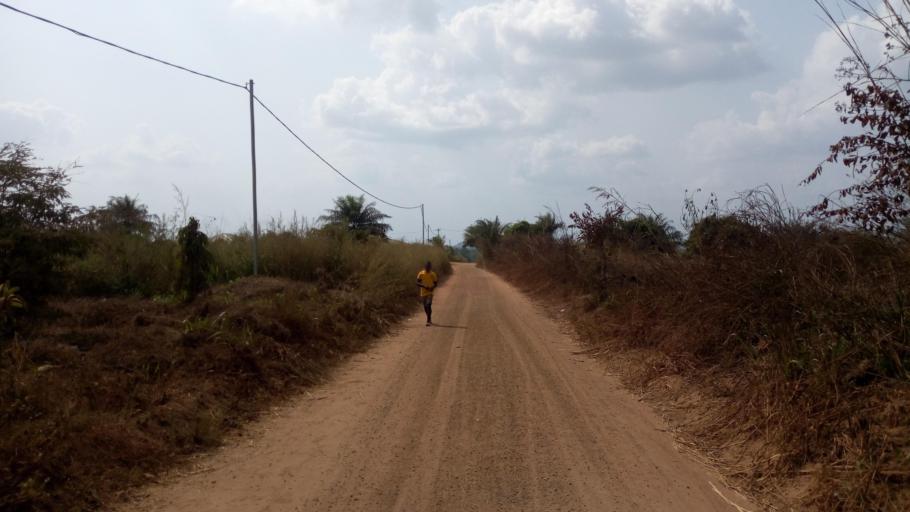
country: SL
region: Southern Province
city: Mogbwemo
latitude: 7.7761
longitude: -12.3001
